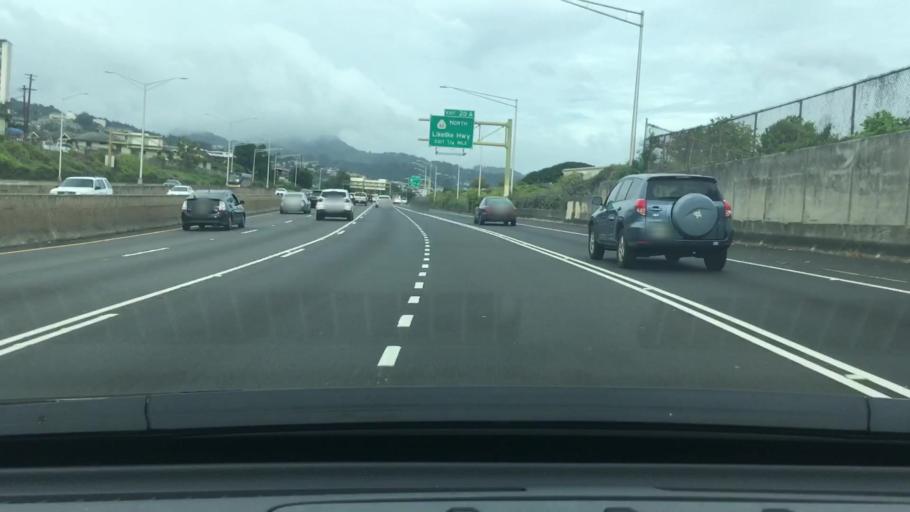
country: US
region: Hawaii
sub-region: Honolulu County
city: Honolulu
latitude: 21.3363
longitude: -157.8814
